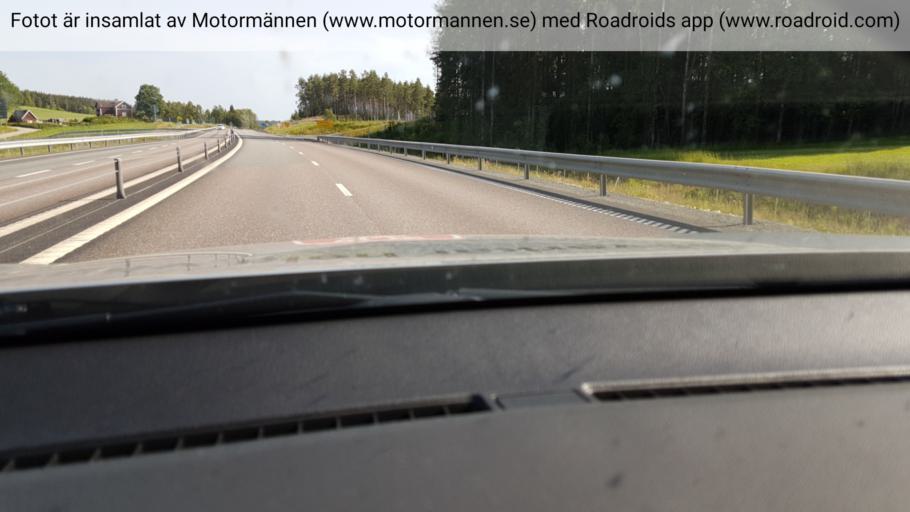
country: SE
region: Joenkoeping
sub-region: Aneby Kommun
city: Aneby
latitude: 57.8146
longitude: 14.8604
